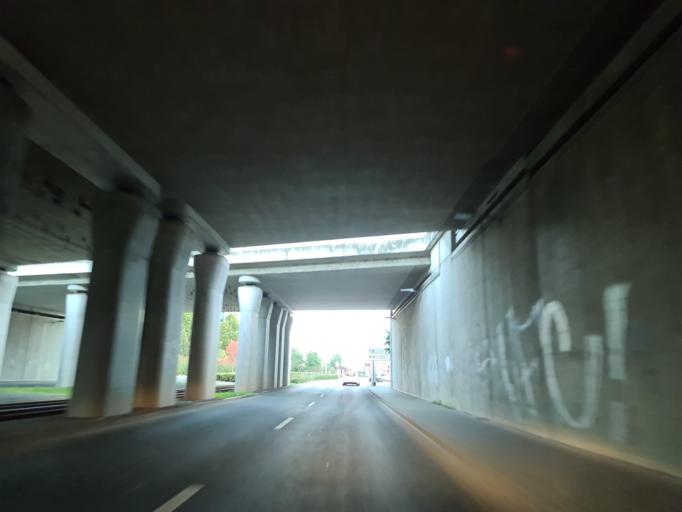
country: DE
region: Saxony
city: Plauen
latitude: 50.5061
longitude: 12.1310
